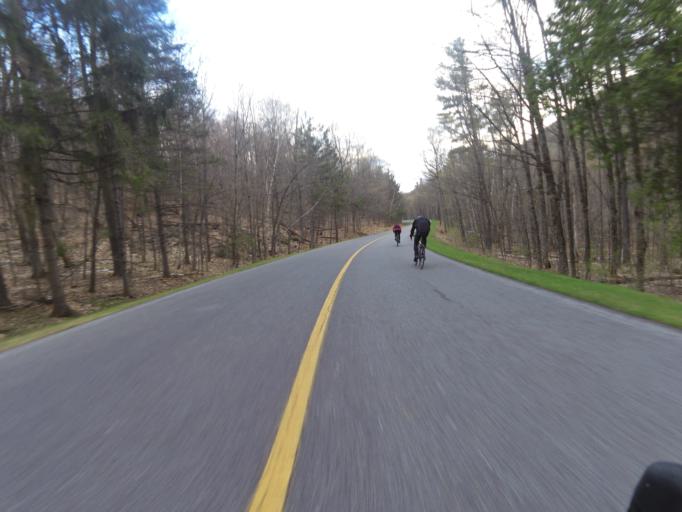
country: CA
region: Quebec
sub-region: Outaouais
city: Gatineau
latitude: 45.4893
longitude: -75.8553
